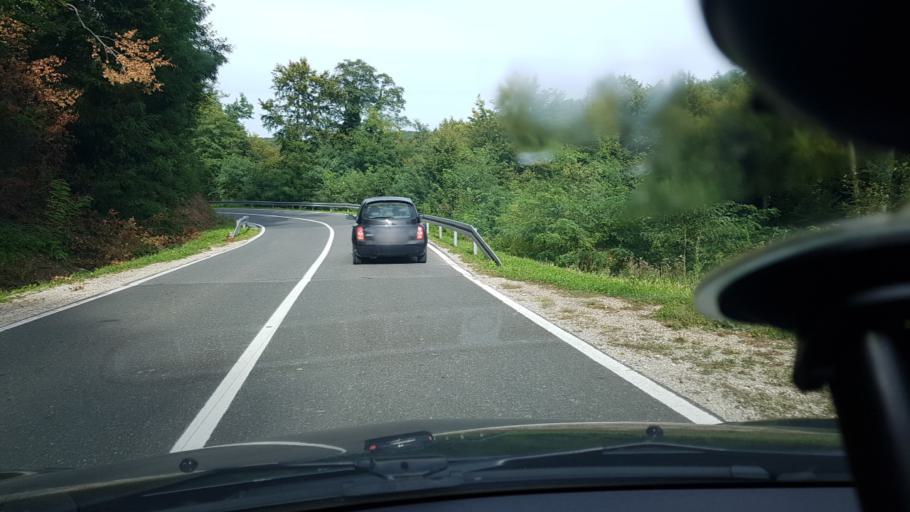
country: HR
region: Varazdinska
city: Ljubescica
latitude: 46.1337
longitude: 16.3585
